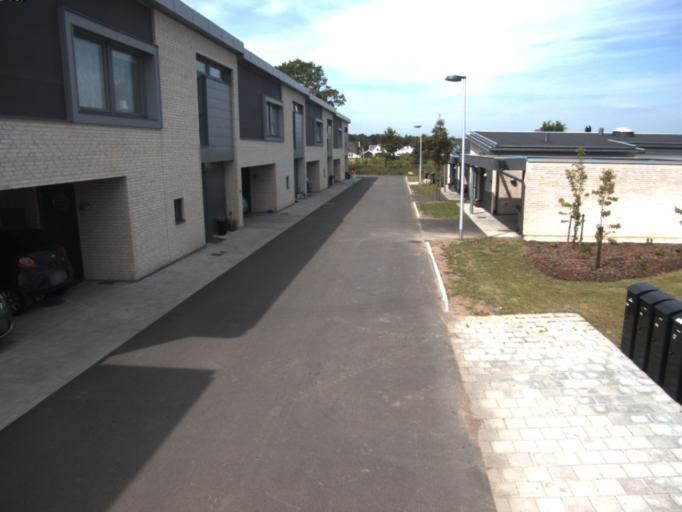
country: SE
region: Skane
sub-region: Helsingborg
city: Helsingborg
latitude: 56.0970
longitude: 12.6624
